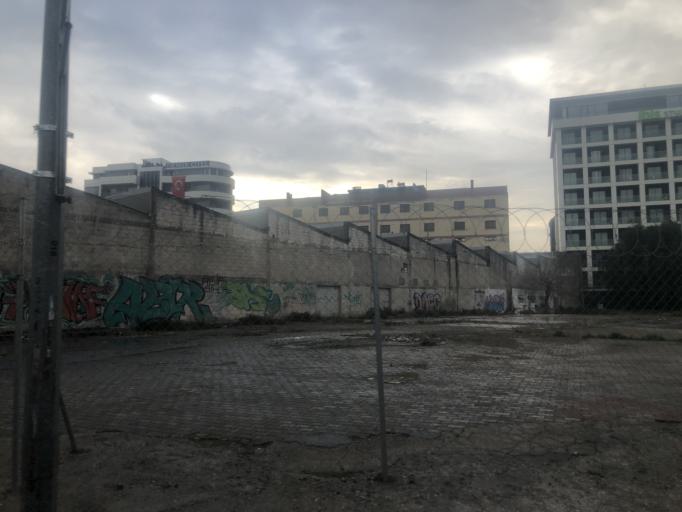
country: TR
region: Izmir
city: Bornova
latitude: 38.4518
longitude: 27.1919
